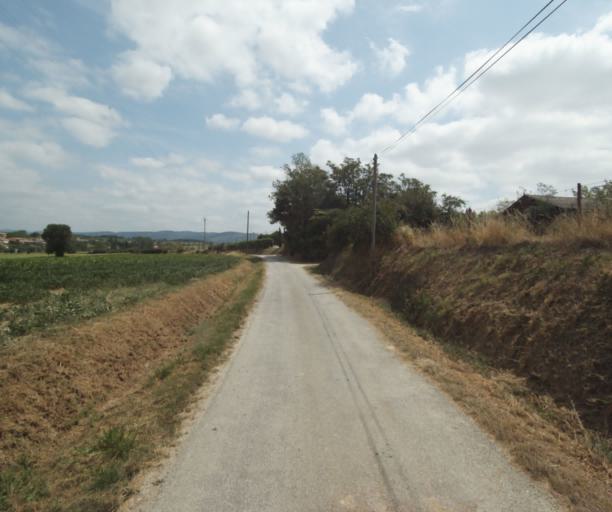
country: FR
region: Midi-Pyrenees
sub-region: Departement de la Haute-Garonne
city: Revel
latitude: 43.4358
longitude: 1.9590
